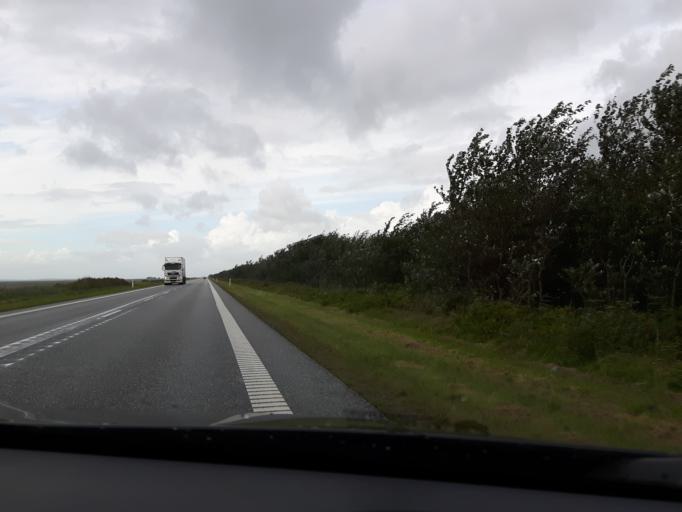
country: DK
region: North Denmark
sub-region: Jammerbugt Kommune
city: Fjerritslev
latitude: 57.0389
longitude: 9.1259
